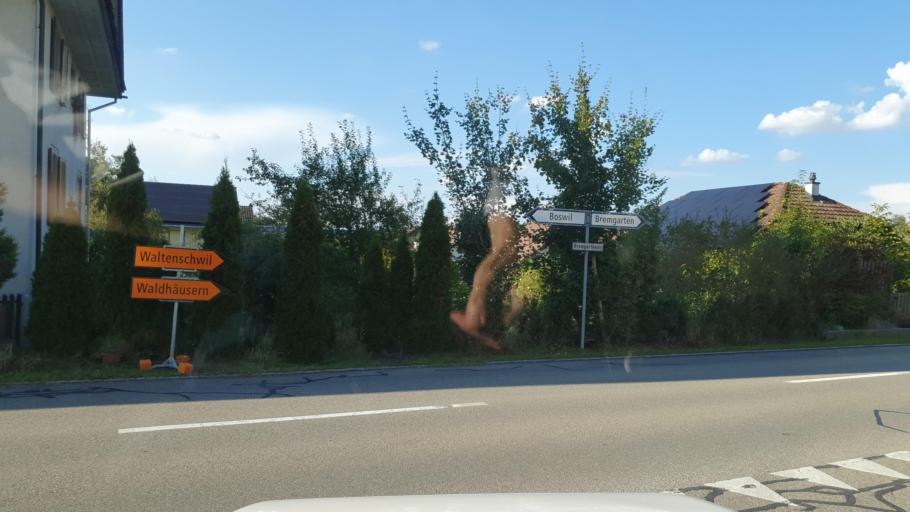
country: CH
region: Aargau
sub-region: Bezirk Muri
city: Waltenschwil
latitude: 47.3109
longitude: 8.3243
